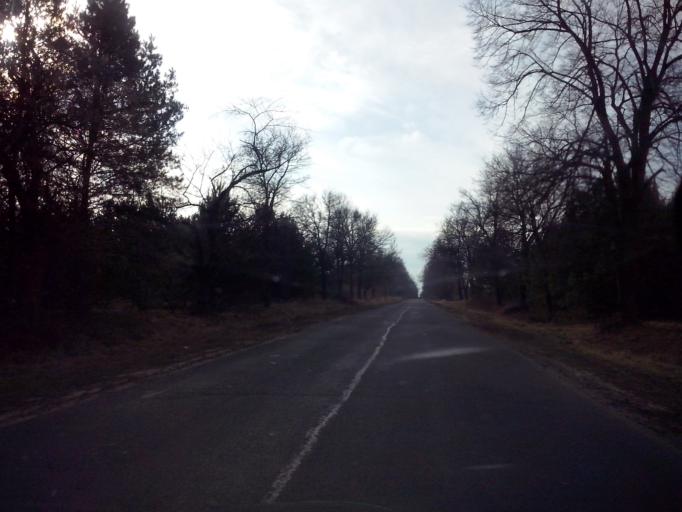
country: PL
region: Subcarpathian Voivodeship
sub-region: Powiat nizanski
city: Harasiuki
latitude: 50.4617
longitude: 22.4249
